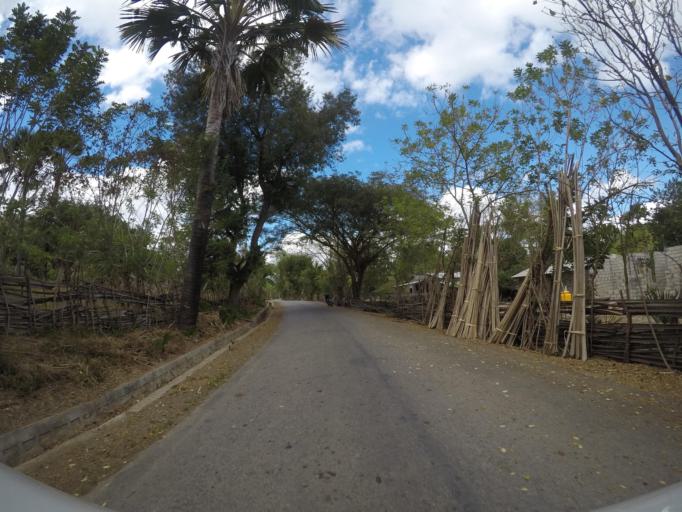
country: TL
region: Lautem
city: Lospalos
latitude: -8.4455
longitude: 126.8243
